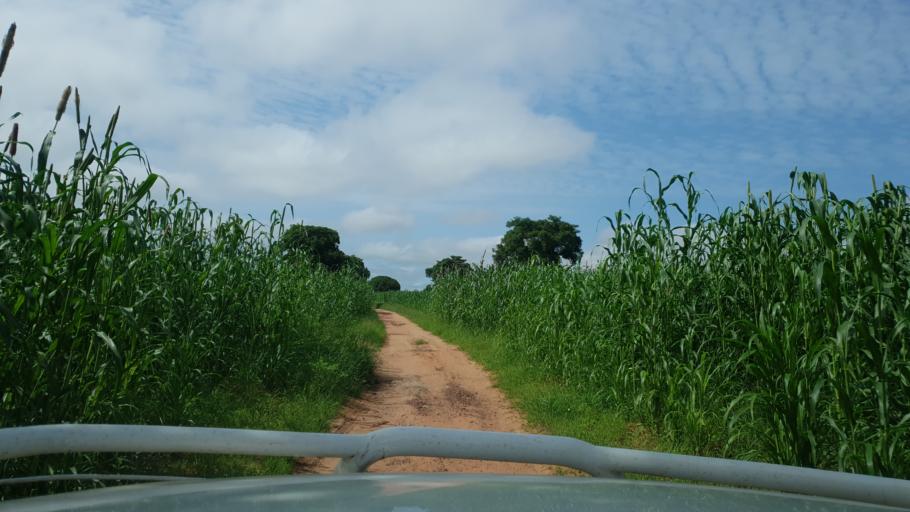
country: ML
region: Segou
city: Baroueli
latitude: 13.4827
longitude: -6.8968
